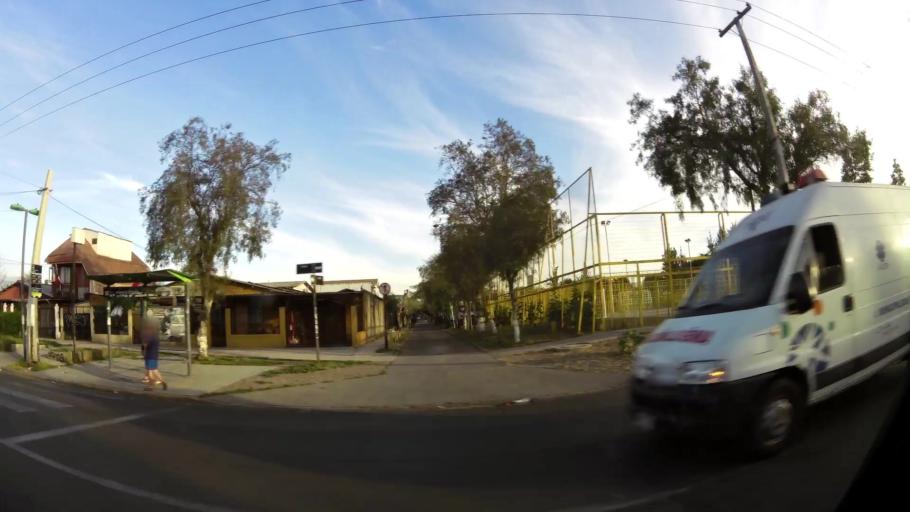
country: CL
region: Santiago Metropolitan
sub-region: Provincia de Santiago
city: Lo Prado
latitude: -33.4503
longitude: -70.7120
